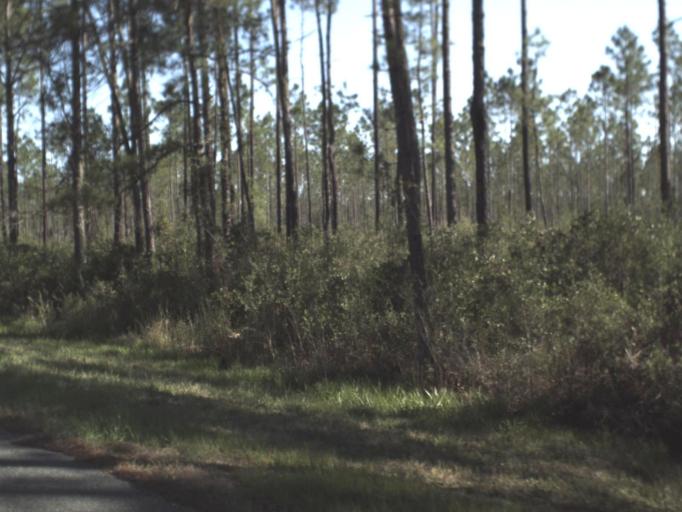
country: US
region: Florida
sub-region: Leon County
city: Woodville
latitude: 30.2387
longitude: -84.0427
